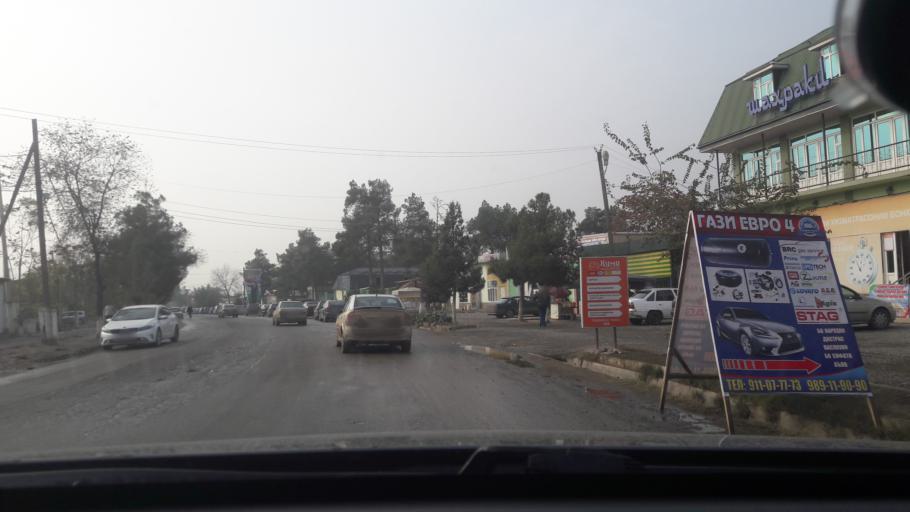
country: TJ
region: Khatlon
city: Abdurahmoni Jomi
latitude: 37.9813
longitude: 68.6957
